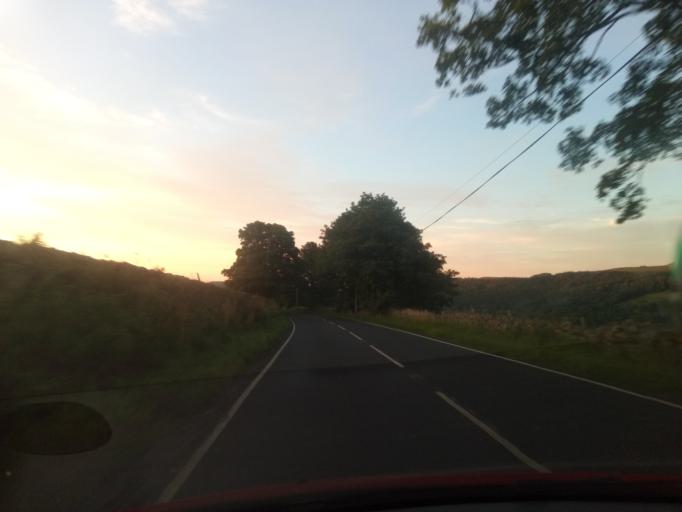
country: GB
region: England
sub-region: Northumberland
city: Bardon Mill
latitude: 54.8816
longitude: -2.3507
